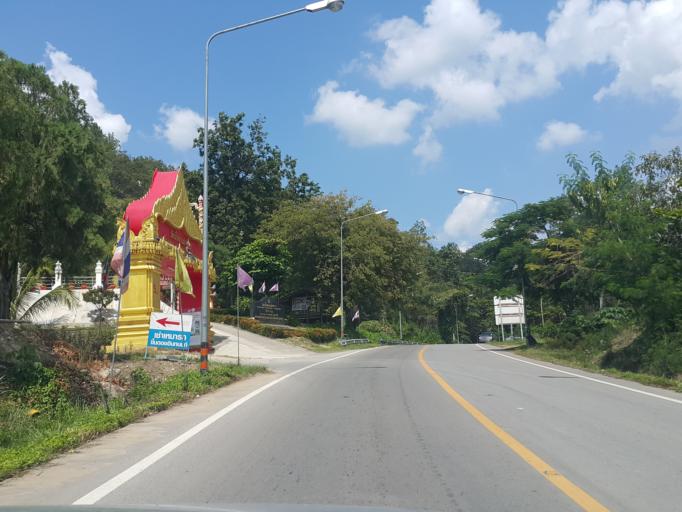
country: TH
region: Chiang Mai
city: Chom Thong
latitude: 18.4947
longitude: 98.6703
